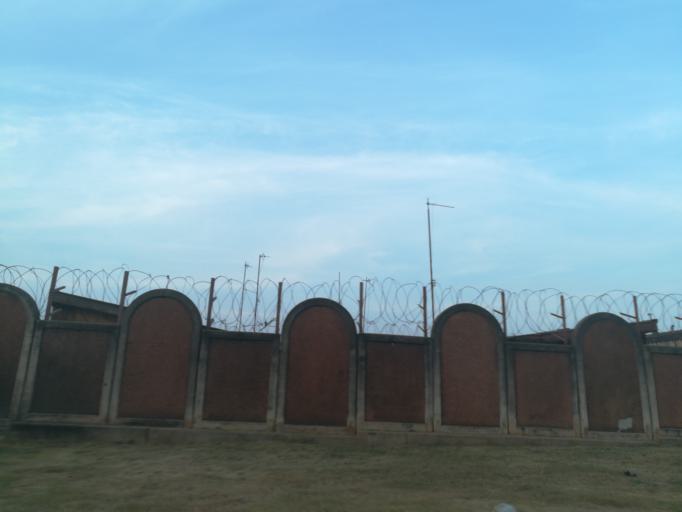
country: NG
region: Abuja Federal Capital Territory
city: Abuja
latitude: 9.0787
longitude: 7.3899
